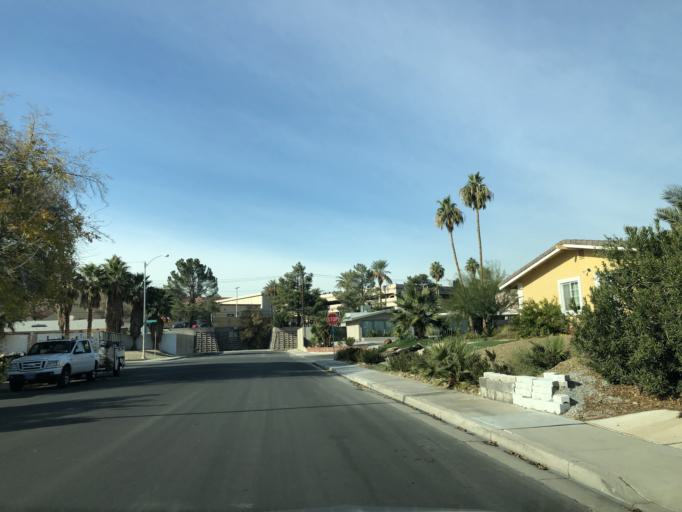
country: US
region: Nevada
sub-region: Clark County
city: Winchester
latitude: 36.1235
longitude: -115.1324
